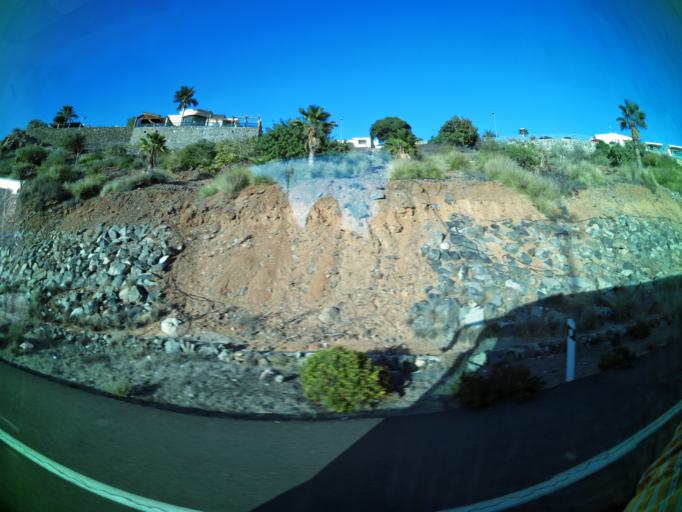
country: ES
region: Canary Islands
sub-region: Provincia de Las Palmas
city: Playa del Ingles
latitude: 27.7735
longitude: -15.5385
